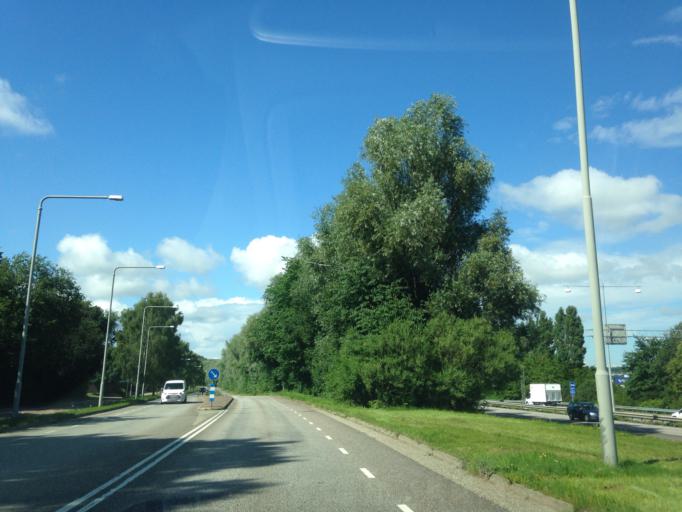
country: SE
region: Vaestra Goetaland
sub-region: Goteborg
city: Goeteborg
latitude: 57.7514
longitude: 11.9908
